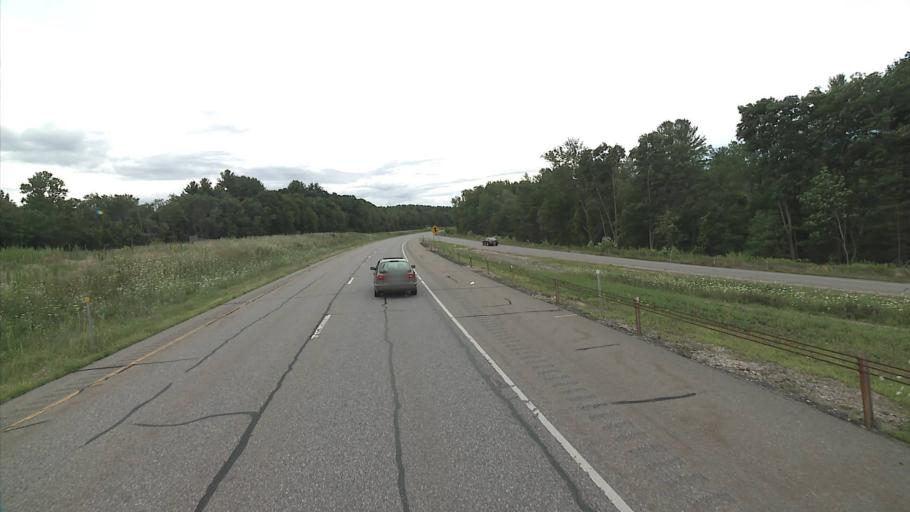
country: US
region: Connecticut
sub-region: Litchfield County
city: Winsted
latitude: 41.8770
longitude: -73.0724
